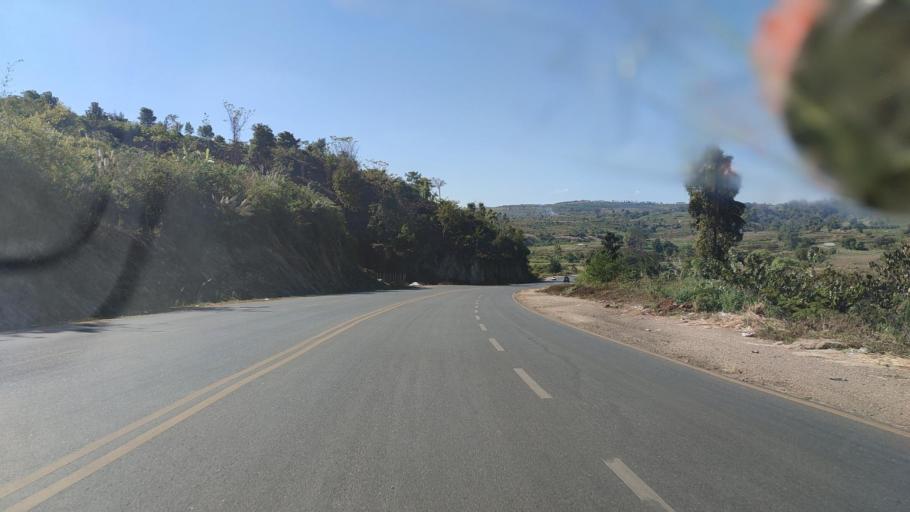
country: MM
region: Mandalay
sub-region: Pyin Oo Lwin District
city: Pyin Oo Lwin
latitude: 22.0784
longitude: 96.5799
